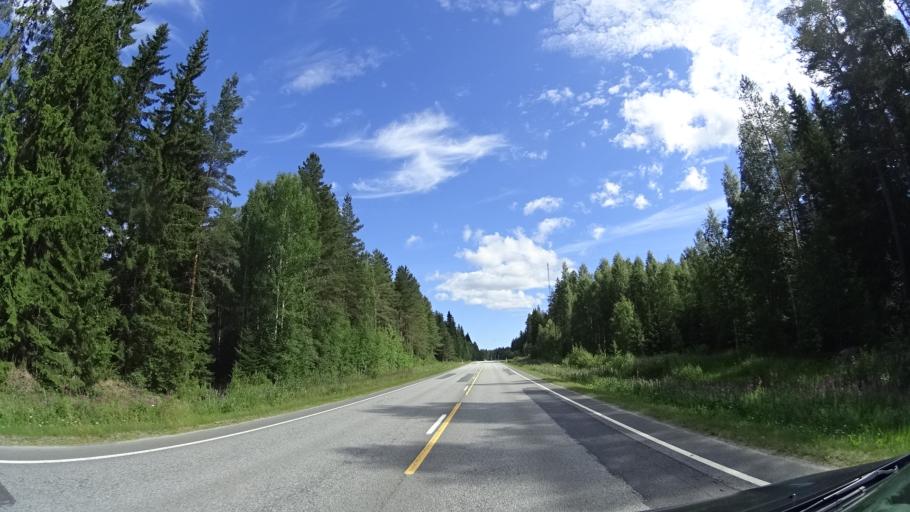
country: FI
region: Pirkanmaa
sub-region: Luoteis-Pirkanmaa
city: Kihnioe
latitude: 62.1479
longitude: 23.1543
